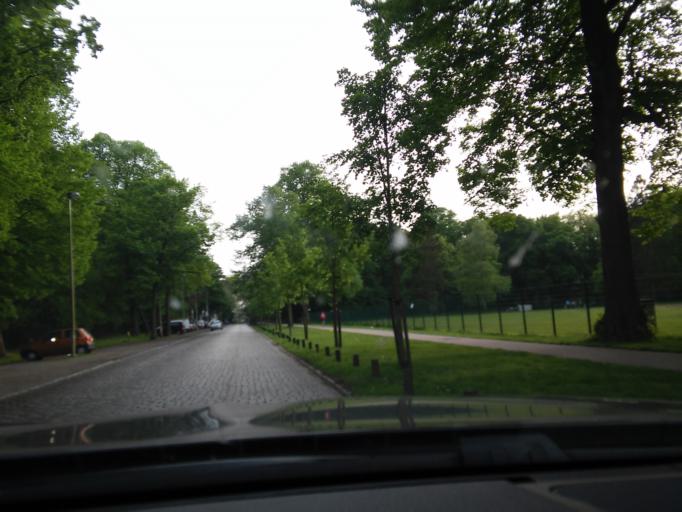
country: BE
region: Flanders
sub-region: Provincie Antwerpen
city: Antwerpen
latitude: 51.1830
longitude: 4.4155
